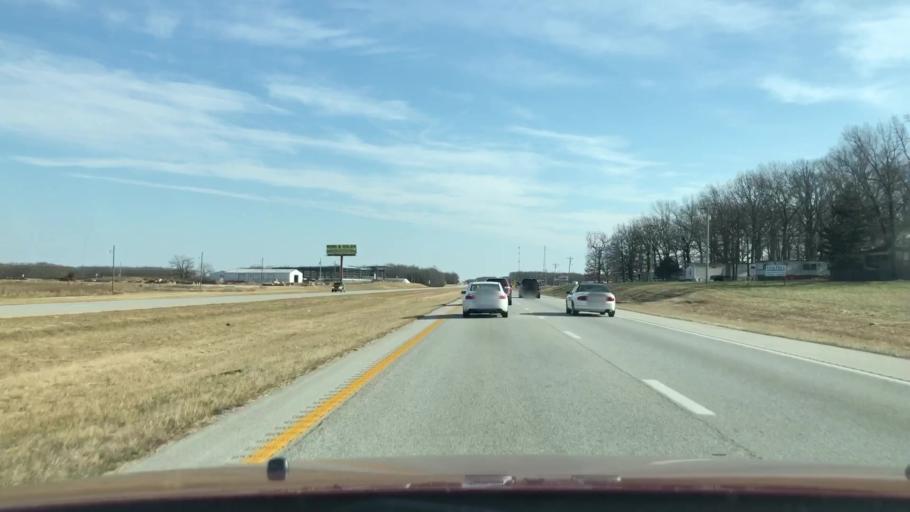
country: US
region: Missouri
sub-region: Webster County
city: Rogersville
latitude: 37.1145
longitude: -93.0350
